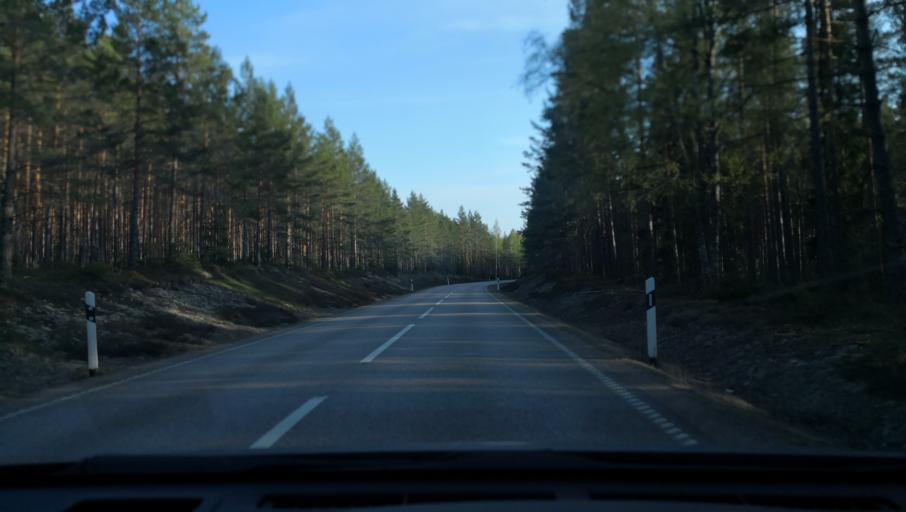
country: SE
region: Uppsala
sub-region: Heby Kommun
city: Tarnsjo
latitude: 60.0884
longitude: 16.8815
